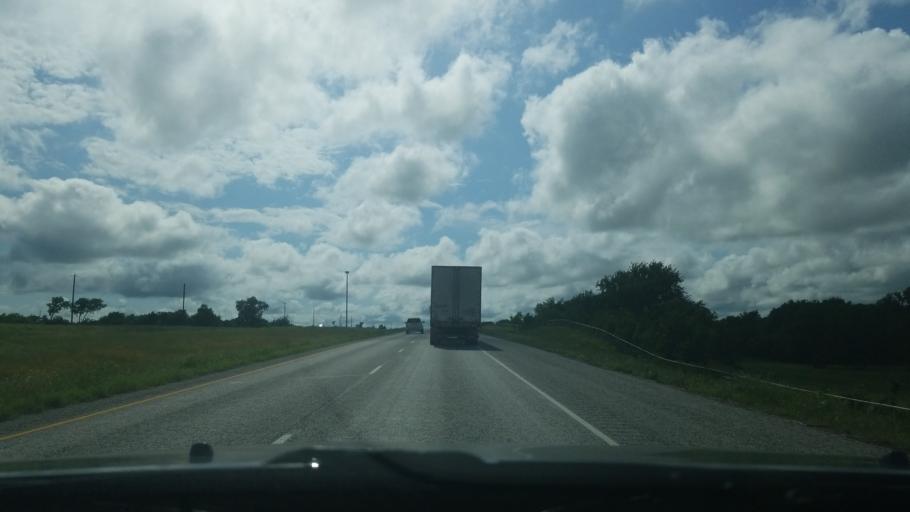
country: US
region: Texas
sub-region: Denton County
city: Krum
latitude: 33.2360
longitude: -97.2721
